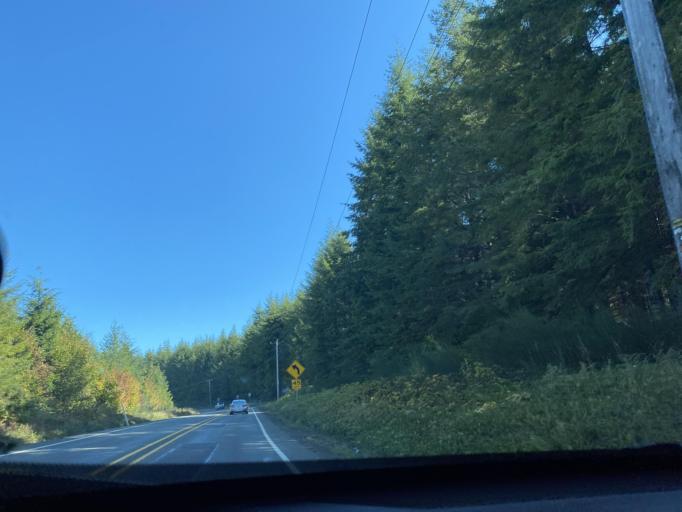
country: US
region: Washington
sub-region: Clallam County
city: Forks
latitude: 47.9540
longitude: -124.4554
